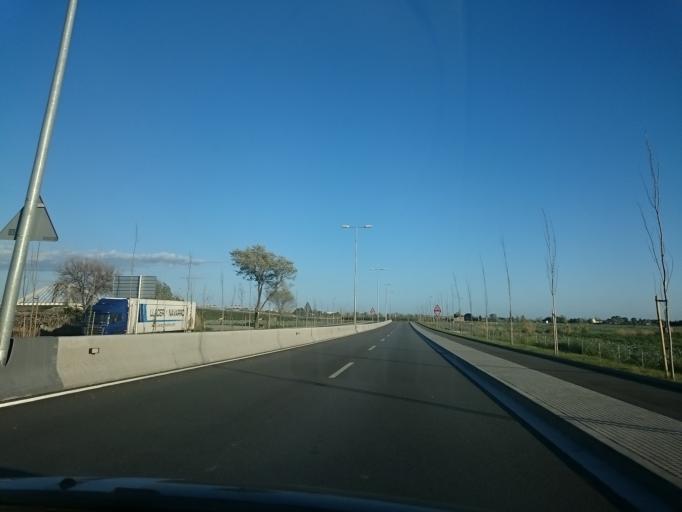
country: ES
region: Catalonia
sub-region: Provincia de Barcelona
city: El Prat de Llobregat
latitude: 41.3229
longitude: 2.1084
